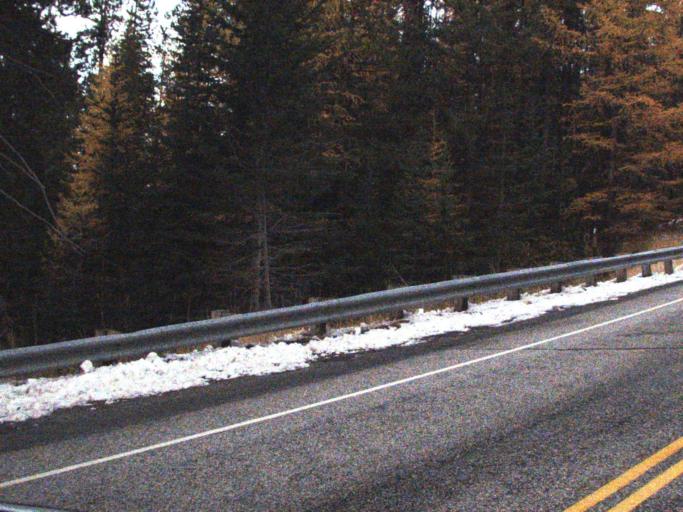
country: US
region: Washington
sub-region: Ferry County
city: Republic
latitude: 48.6069
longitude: -118.4637
